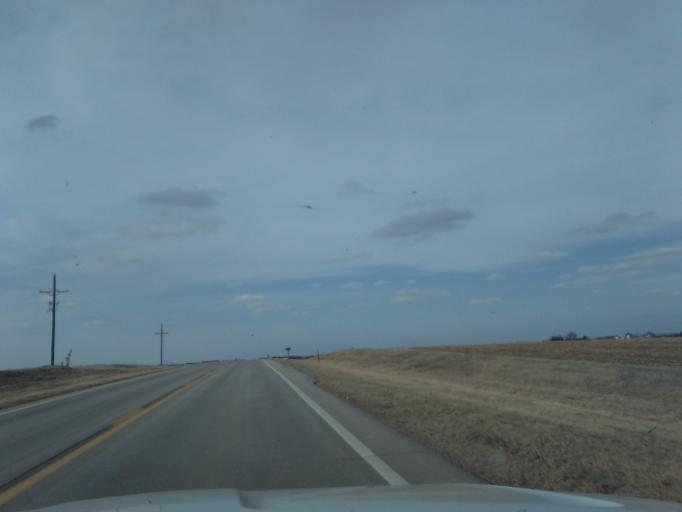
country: US
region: Nebraska
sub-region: Saline County
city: Wilber
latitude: 40.3149
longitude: -96.9162
